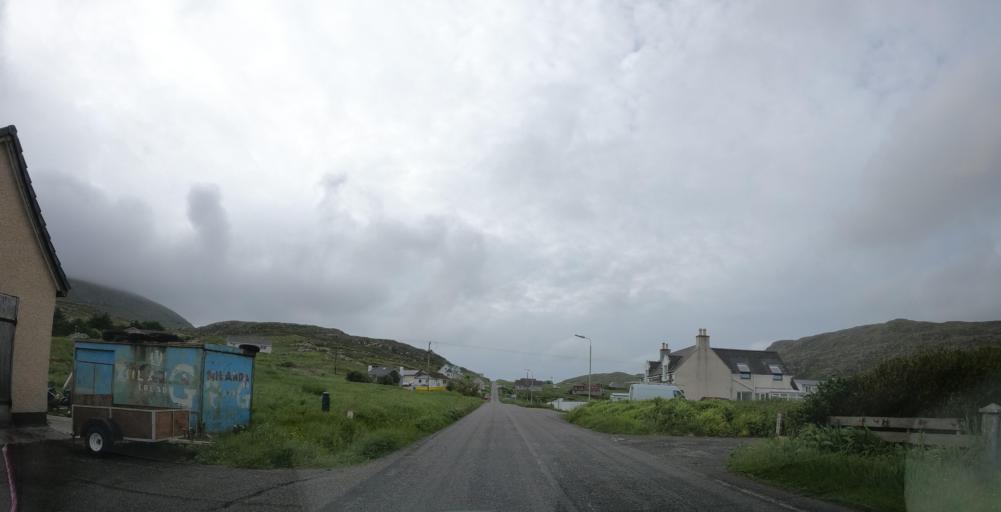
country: GB
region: Scotland
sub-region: Eilean Siar
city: Barra
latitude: 56.9583
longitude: -7.5039
